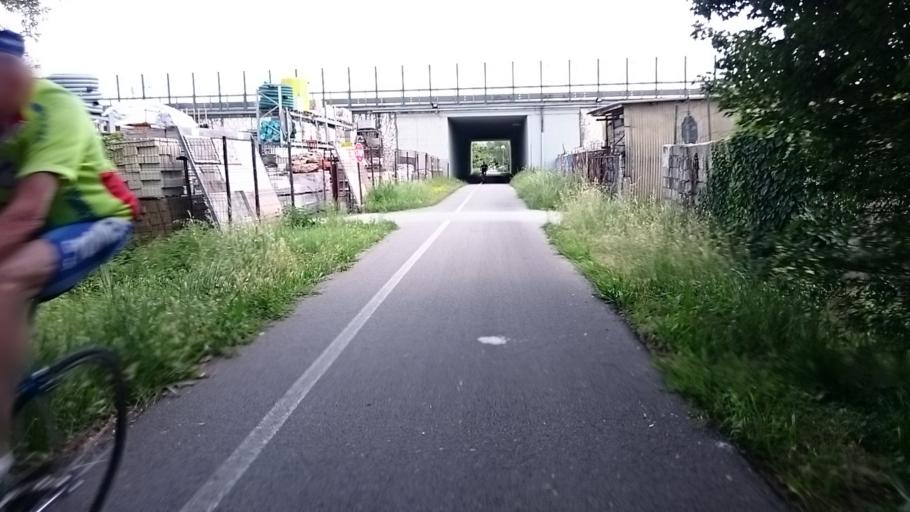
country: IT
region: Veneto
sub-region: Provincia di Vicenza
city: Arcugnano-Torri
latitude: 45.5170
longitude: 11.5673
